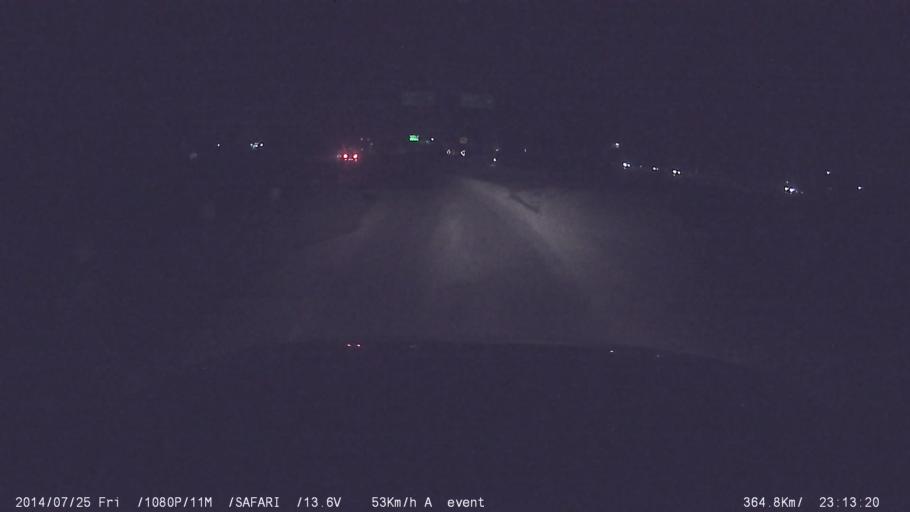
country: IN
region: Tamil Nadu
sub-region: Coimbatore
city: Madukkarai
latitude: 10.8949
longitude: 76.9356
